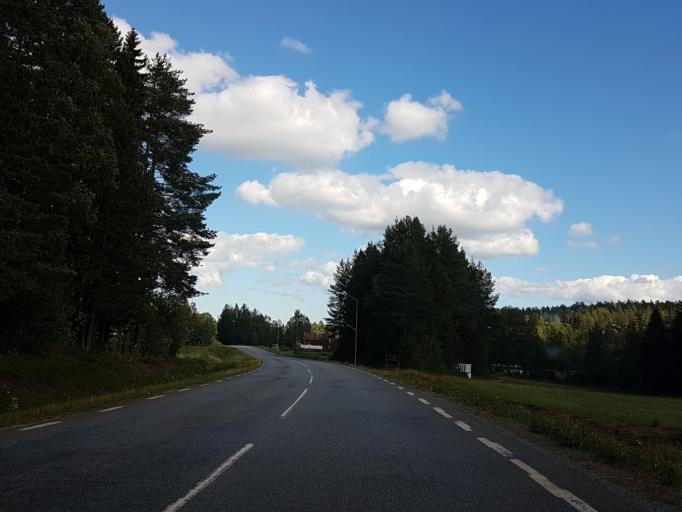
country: SE
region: Vaesterbotten
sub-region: Skelleftea Kommun
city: Burtraesk
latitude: 64.2645
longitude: 20.4795
